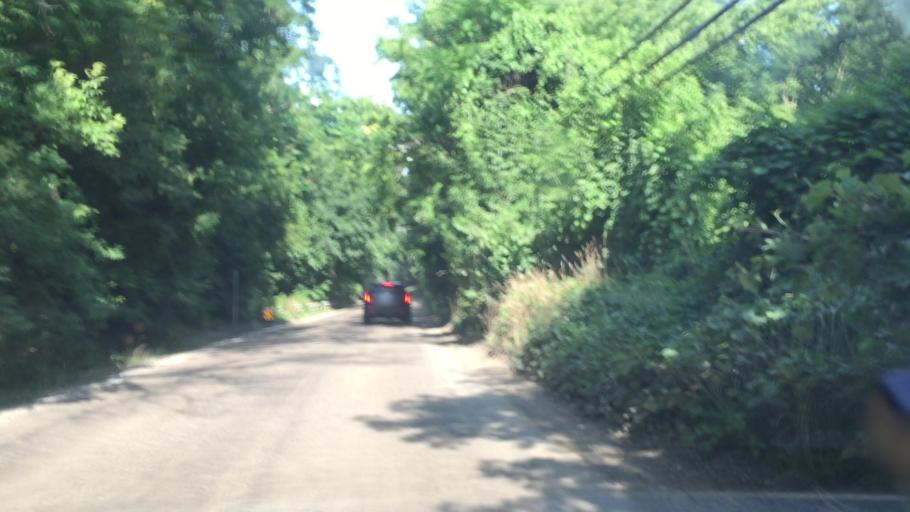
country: US
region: Michigan
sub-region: Oakland County
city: Franklin
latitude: 42.5296
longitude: -83.3085
